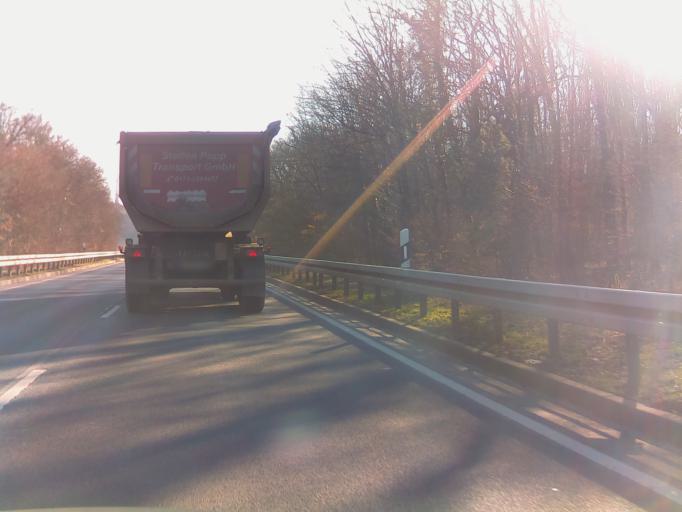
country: DE
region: Bavaria
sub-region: Regierungsbezirk Unterfranken
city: Munnerstadt
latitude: 50.2297
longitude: 10.1670
